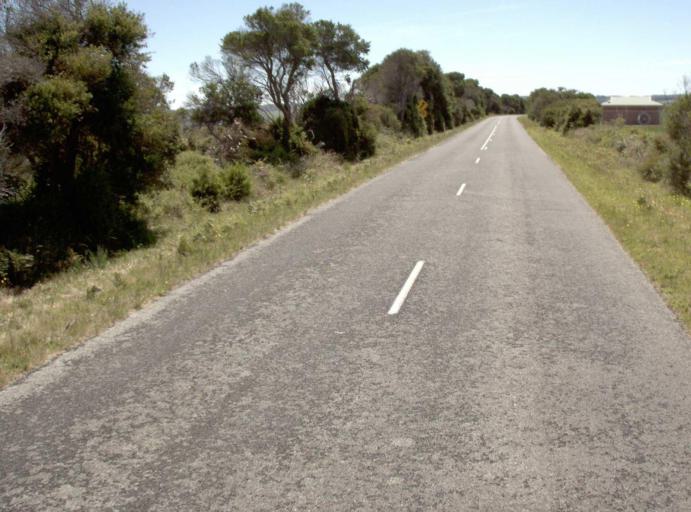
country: AU
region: Victoria
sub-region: Bass Coast
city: North Wonthaggi
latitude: -38.8141
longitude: 146.1031
